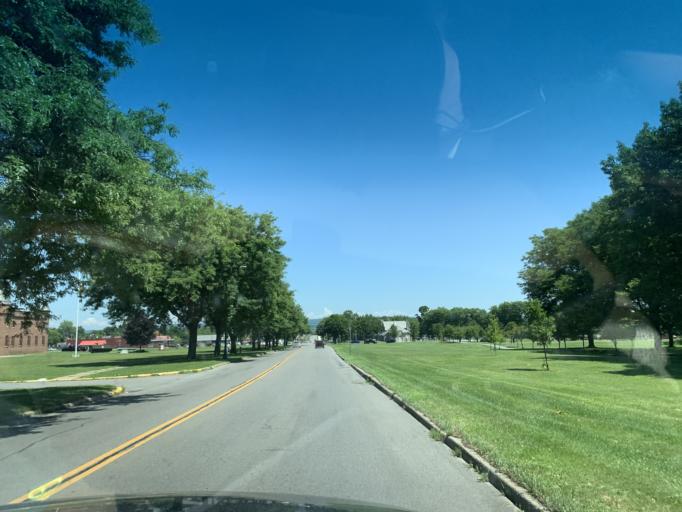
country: US
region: New York
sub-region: Oneida County
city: Utica
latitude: 43.0781
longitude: -75.2079
